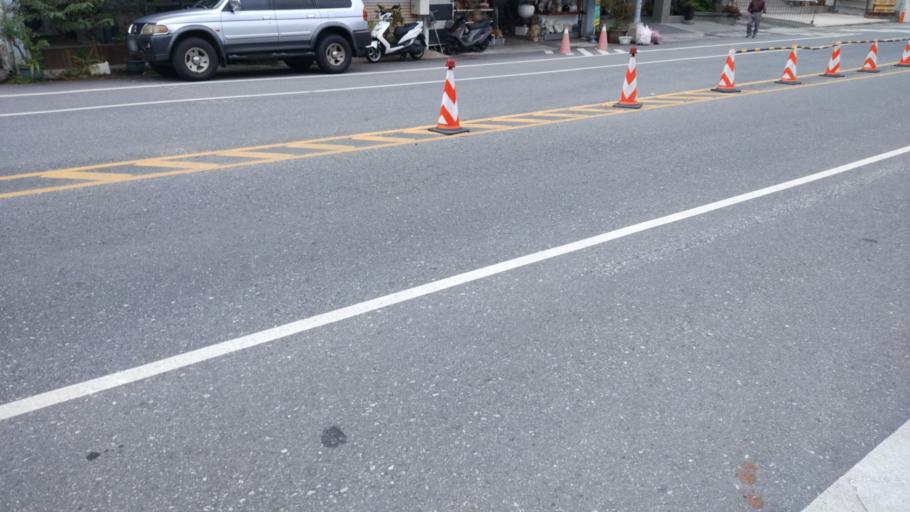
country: TW
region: Taiwan
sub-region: Hualien
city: Hualian
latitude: 23.9290
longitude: 121.5059
